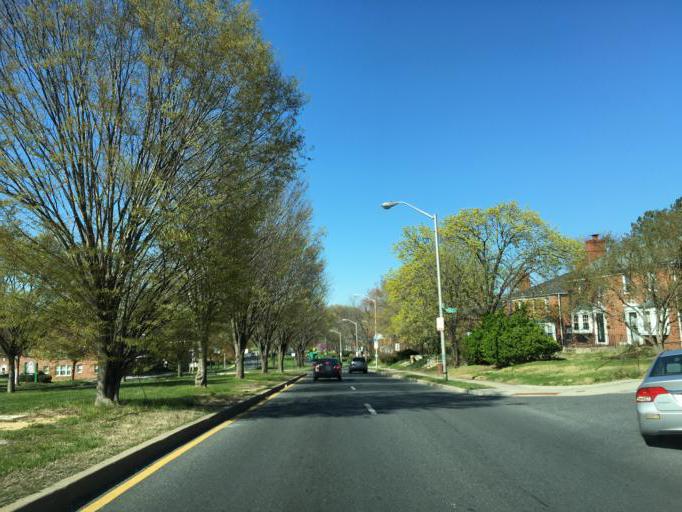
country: US
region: Maryland
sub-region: City of Baltimore
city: Baltimore
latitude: 39.3419
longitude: -76.5930
